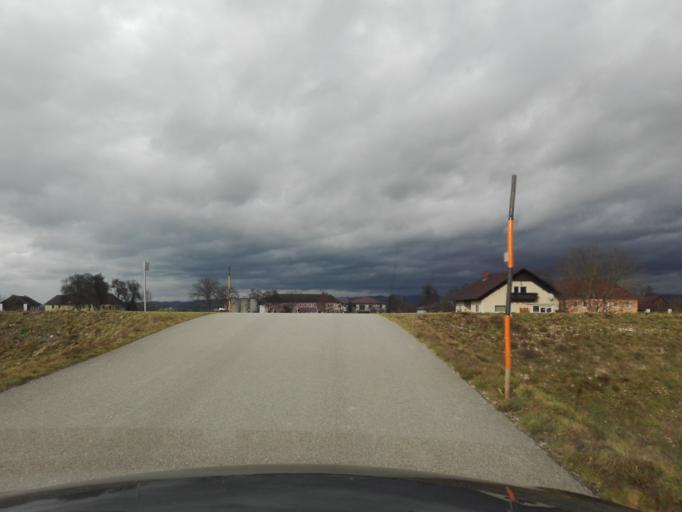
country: AT
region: Lower Austria
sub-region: Politischer Bezirk Amstetten
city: Strengberg
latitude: 48.1796
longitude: 14.6884
